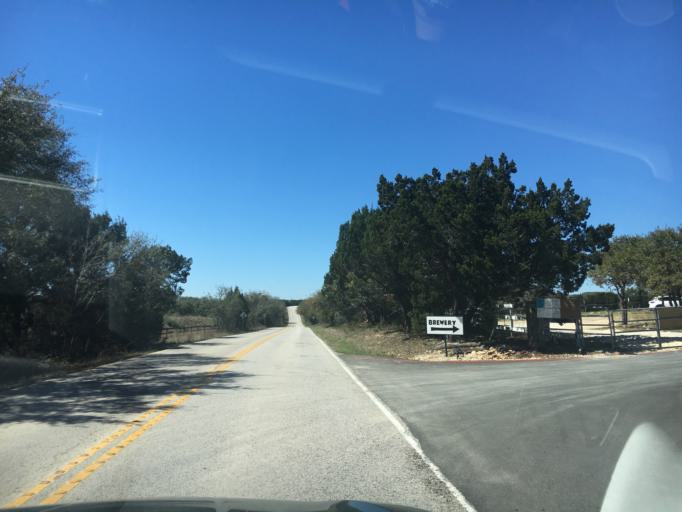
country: US
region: Texas
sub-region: Hays County
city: Dripping Springs
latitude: 30.2915
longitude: -98.0784
